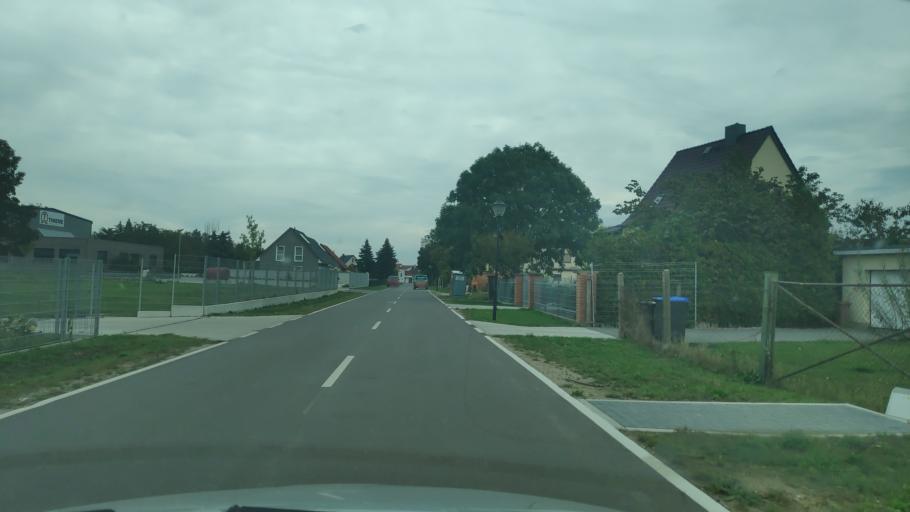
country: DE
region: Saxony-Anhalt
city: Barby
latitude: 51.9625
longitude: 11.8852
